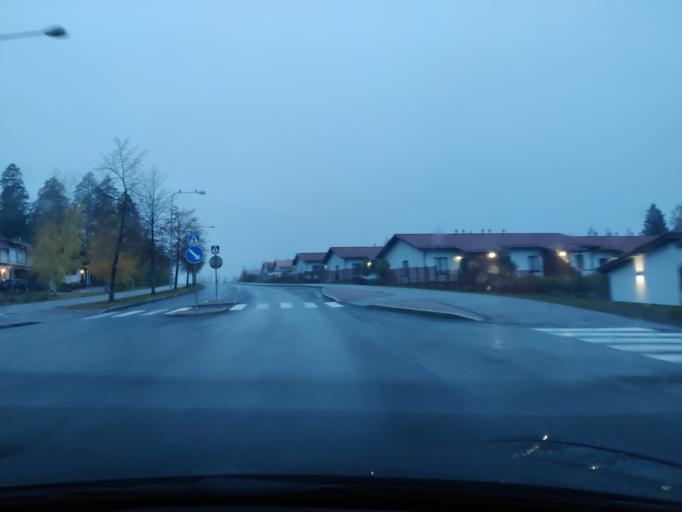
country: FI
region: Northern Savo
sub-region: Kuopio
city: Kuopio
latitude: 62.8267
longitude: 27.6866
